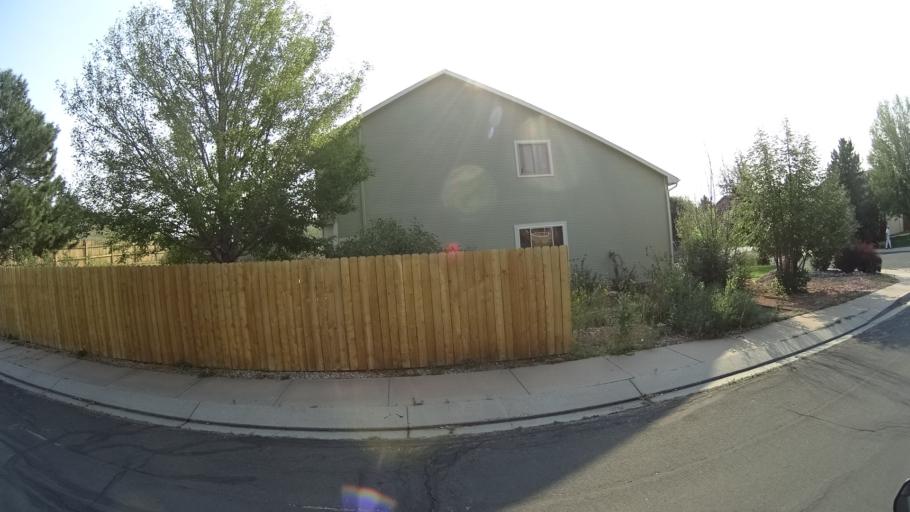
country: US
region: Colorado
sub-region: El Paso County
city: Colorado Springs
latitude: 38.8144
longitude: -104.8489
